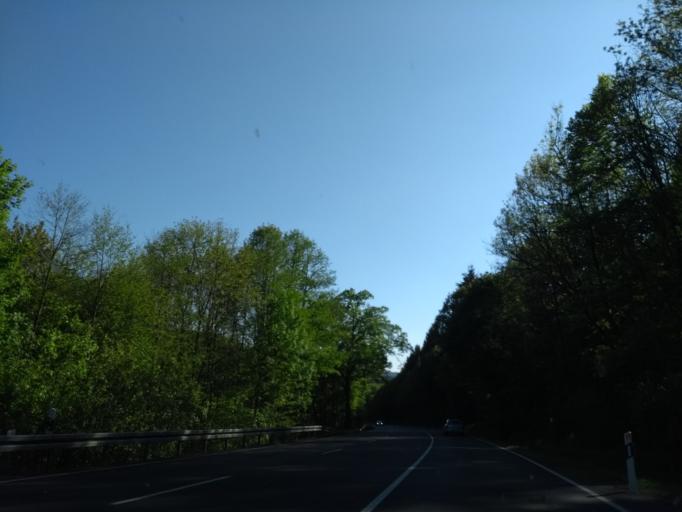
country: DE
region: Hesse
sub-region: Regierungsbezirk Giessen
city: Biedenkopf
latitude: 50.9381
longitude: 8.5376
